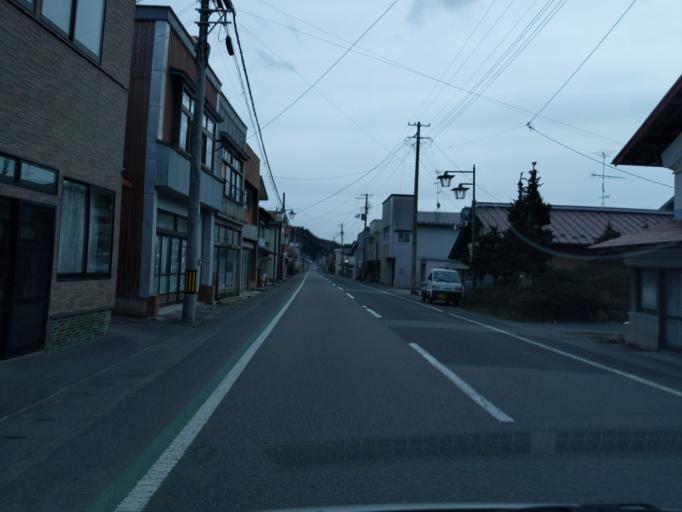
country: JP
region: Iwate
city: Mizusawa
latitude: 39.0388
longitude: 141.2943
